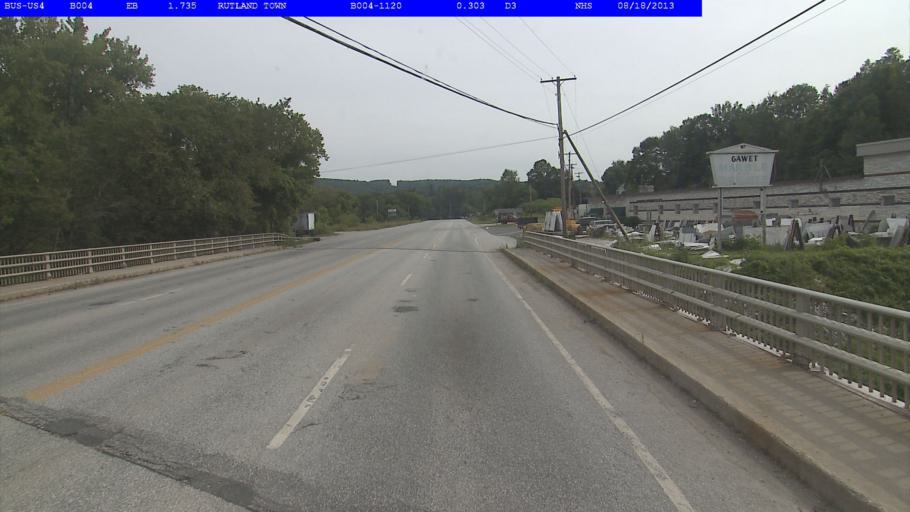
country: US
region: Vermont
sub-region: Rutland County
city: West Rutland
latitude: 43.6007
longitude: -73.0189
